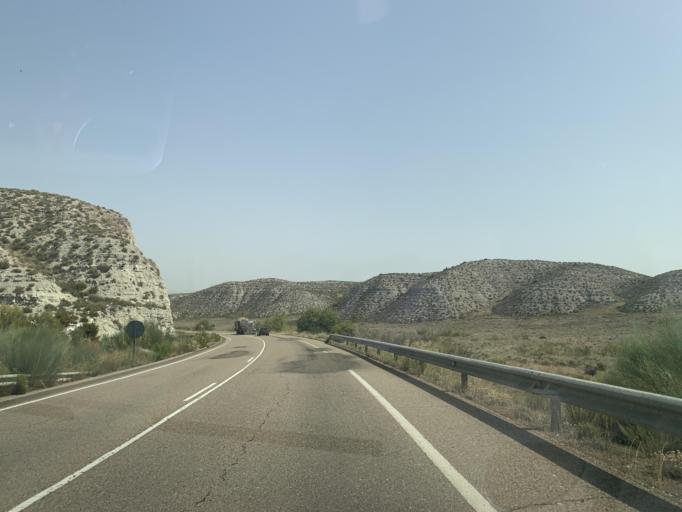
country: ES
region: Aragon
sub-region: Provincia de Zaragoza
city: El Burgo de Ebro
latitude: 41.5279
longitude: -0.6986
